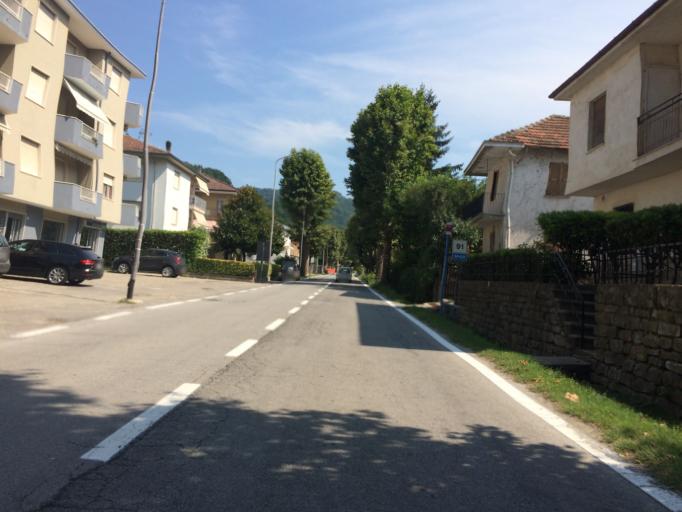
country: IT
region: Piedmont
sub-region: Provincia di Cuneo
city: Cortemilia
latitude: 44.5763
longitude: 8.1978
